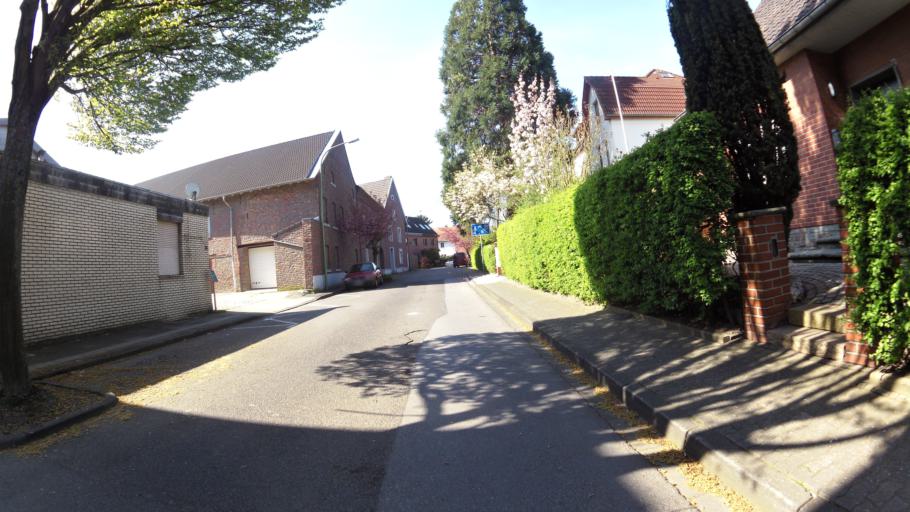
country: DE
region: North Rhine-Westphalia
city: Baesweiler
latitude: 50.9246
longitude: 6.1678
